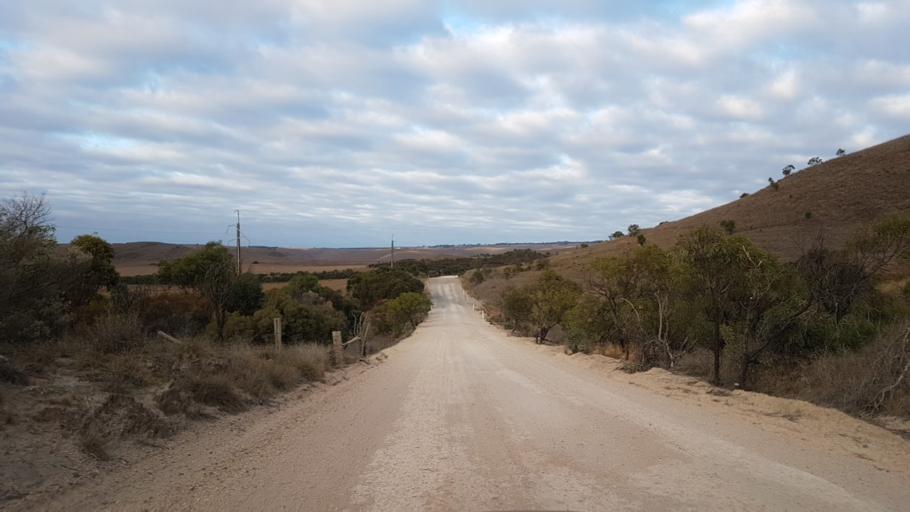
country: AU
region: South Australia
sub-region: Mount Barker
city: Callington
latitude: -35.0979
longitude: 139.0071
